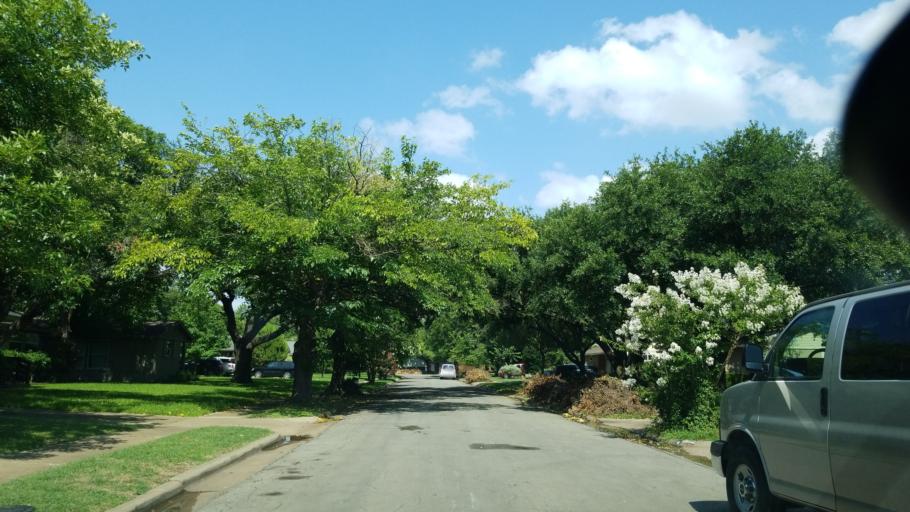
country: US
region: Texas
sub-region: Dallas County
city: Farmers Branch
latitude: 32.8838
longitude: -96.8654
